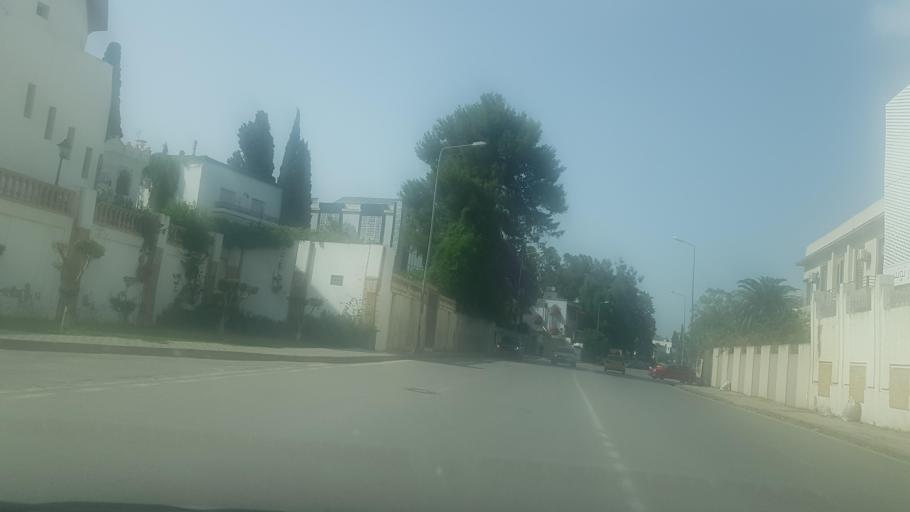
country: TN
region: Tunis
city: Tunis
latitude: 36.8239
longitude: 10.1787
